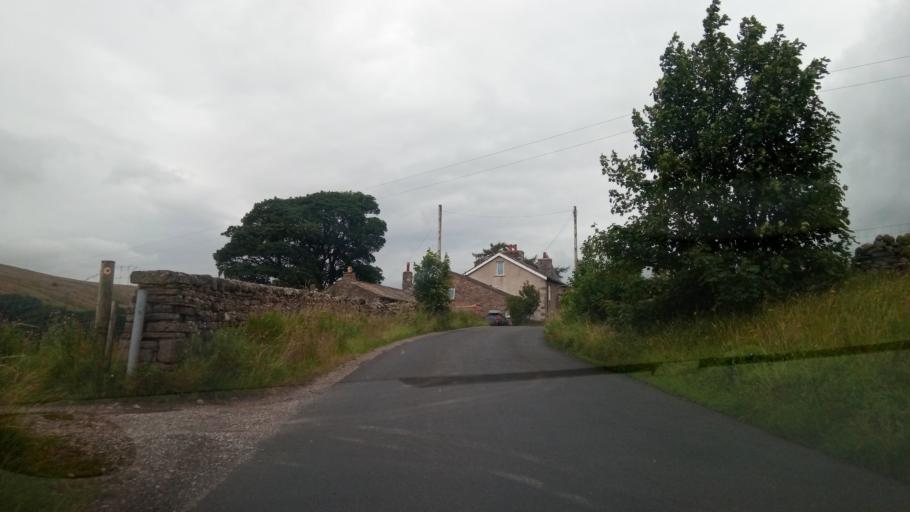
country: GB
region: England
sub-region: Cumbria
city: Kirkby Stephen
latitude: 54.3996
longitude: -2.3357
